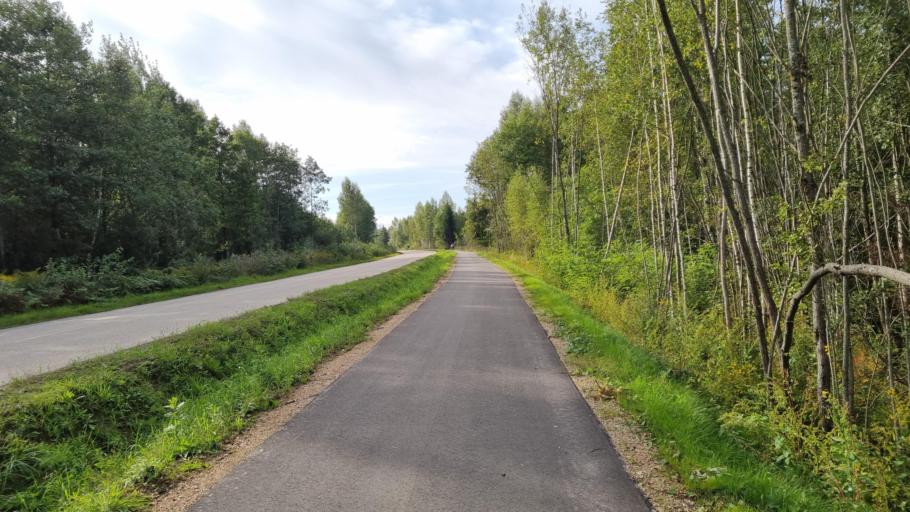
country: LV
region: Lecava
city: Iecava
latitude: 56.6985
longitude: 24.0810
